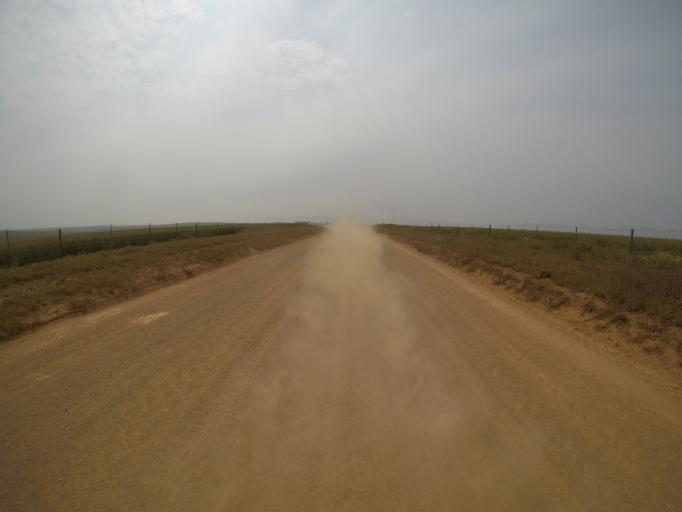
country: ZA
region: Western Cape
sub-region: City of Cape Town
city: Kraaifontein
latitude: -33.7158
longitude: 18.6824
